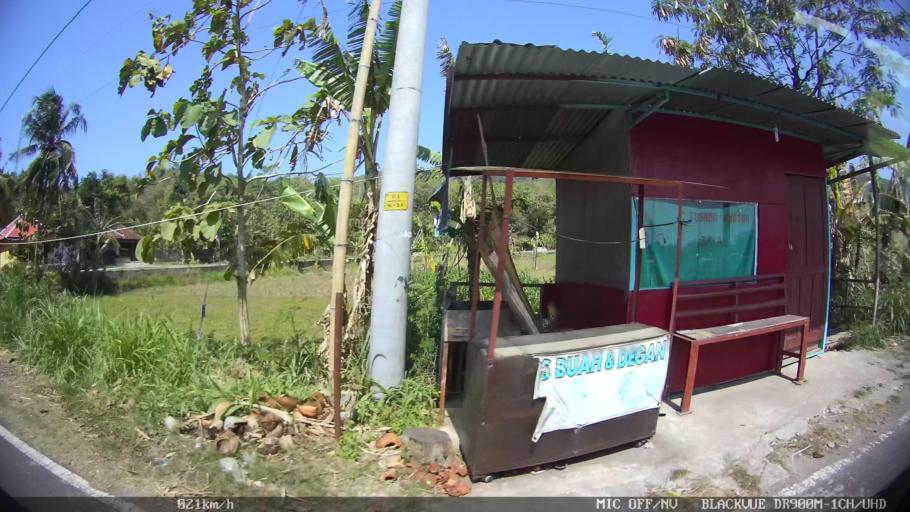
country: ID
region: Daerah Istimewa Yogyakarta
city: Pundong
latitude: -7.9644
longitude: 110.3558
